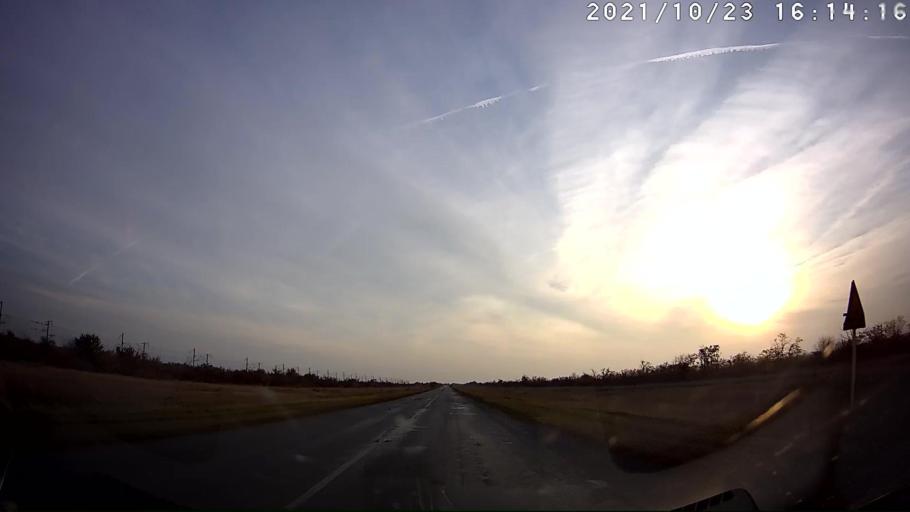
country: RU
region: Volgograd
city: Kotel'nikovo
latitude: 47.9484
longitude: 43.6069
